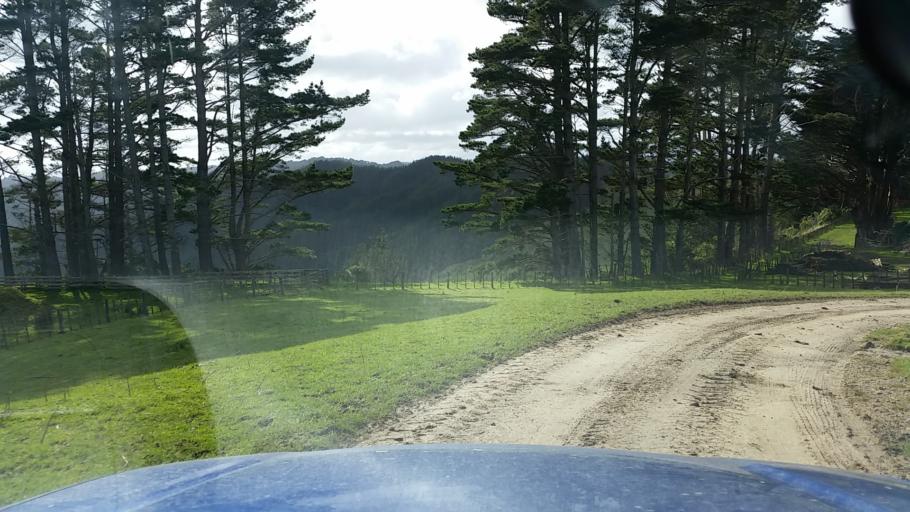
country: NZ
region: Taranaki
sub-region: South Taranaki District
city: Patea
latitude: -39.6579
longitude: 174.5694
